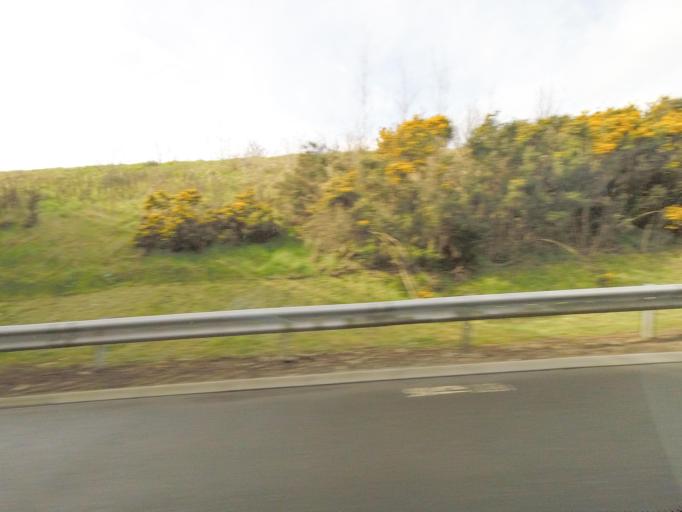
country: IE
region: Leinster
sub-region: Kilkenny
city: Mooncoin
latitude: 52.3737
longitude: -7.1670
